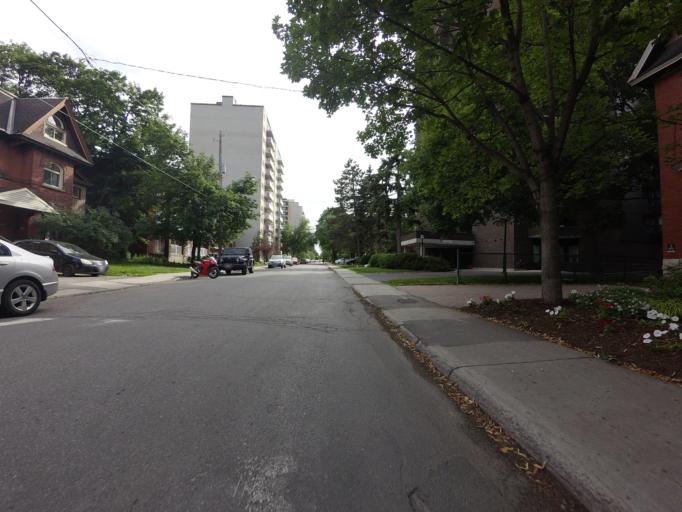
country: CA
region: Ontario
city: Ottawa
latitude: 45.4194
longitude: -75.6869
